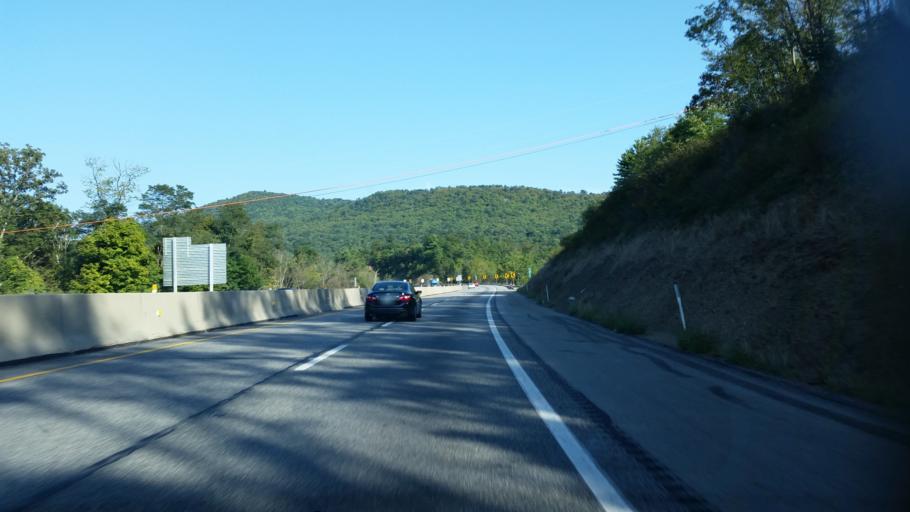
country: US
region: Pennsylvania
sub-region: Fulton County
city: McConnellsburg
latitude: 40.0683
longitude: -77.9288
